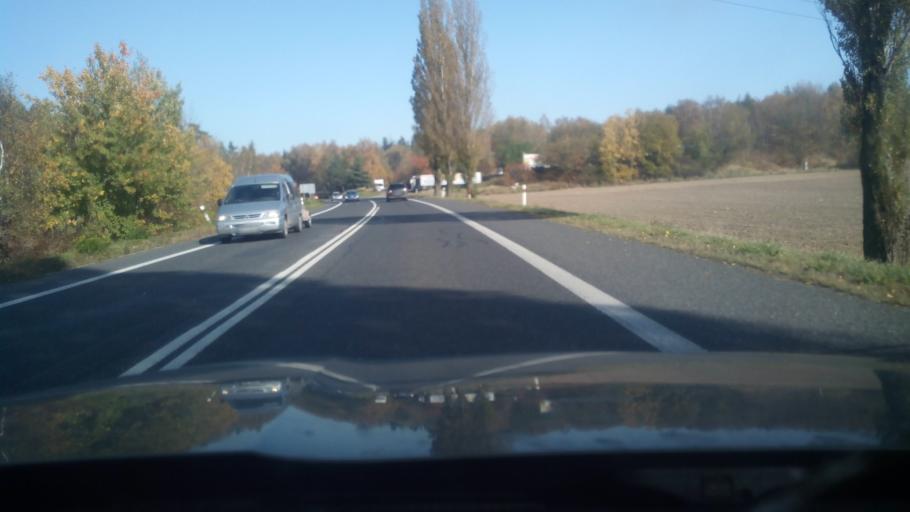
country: CZ
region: Central Bohemia
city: Milin
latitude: 49.6544
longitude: 14.0584
